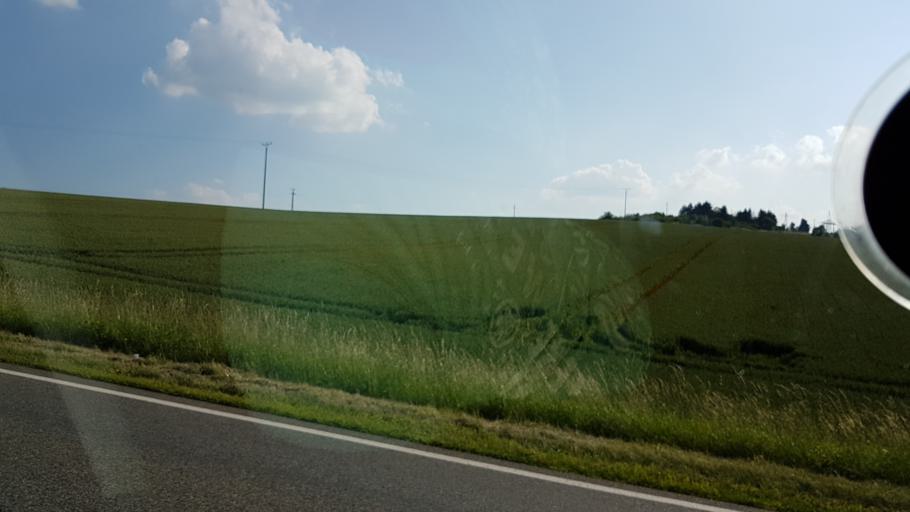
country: DE
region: Rheinland-Pfalz
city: Meisenheim
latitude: 49.7089
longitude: 7.6618
